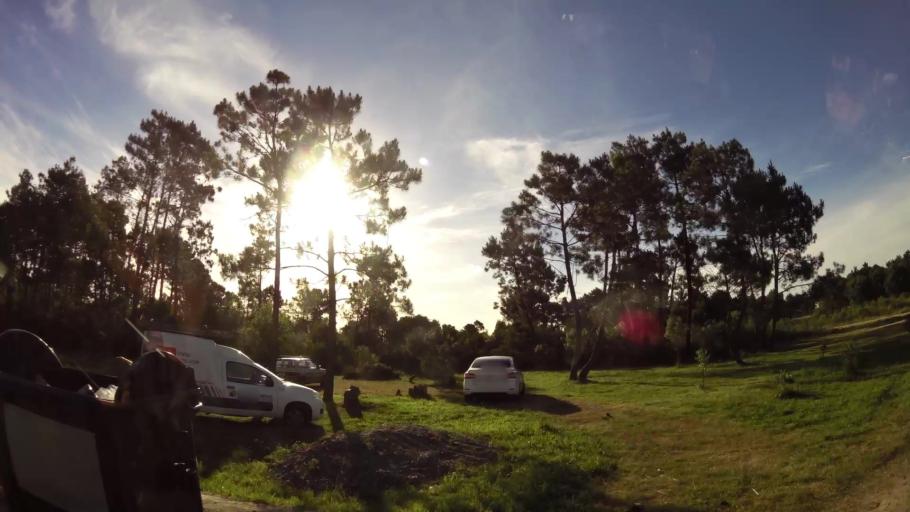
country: UY
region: Canelones
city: Empalme Olmos
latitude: -34.7662
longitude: -55.8582
